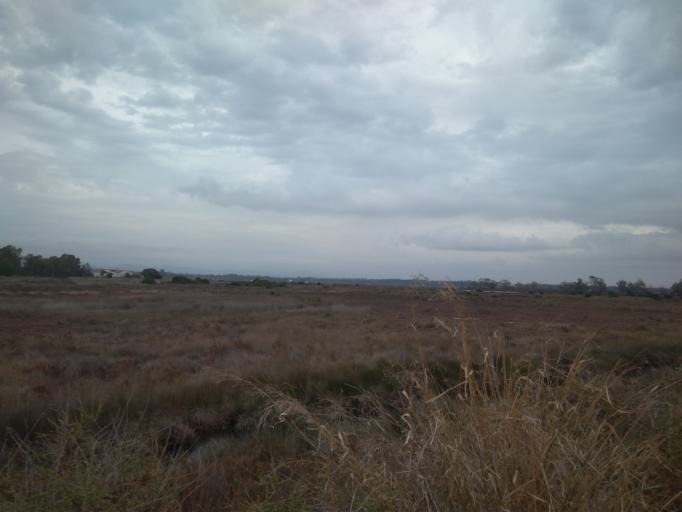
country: PT
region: Faro
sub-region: Loule
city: Almancil
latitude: 37.0218
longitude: -8.0083
